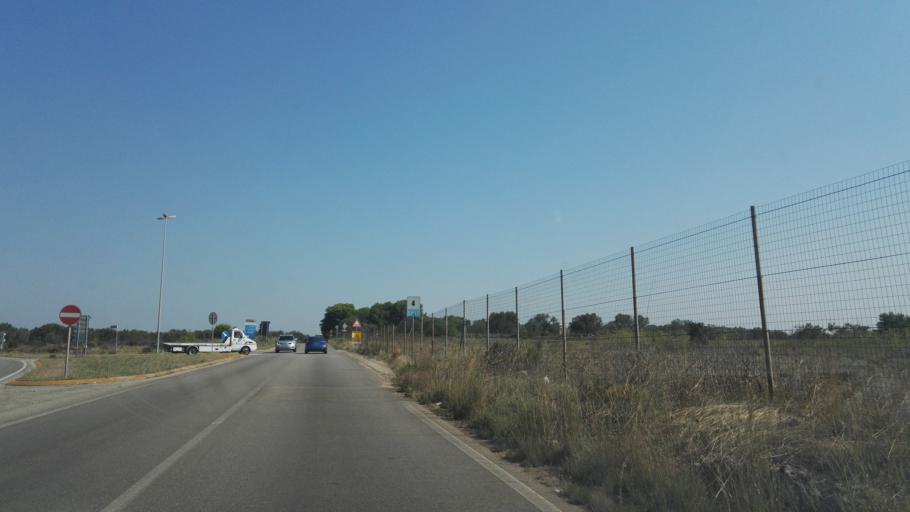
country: IT
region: Apulia
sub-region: Provincia di Lecce
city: Nardo
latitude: 40.1365
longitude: 18.0190
